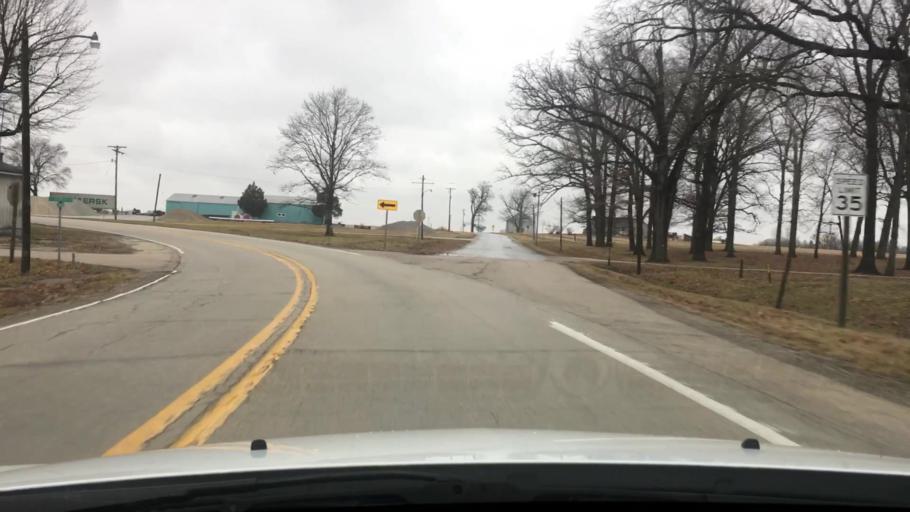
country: US
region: Illinois
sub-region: Iroquois County
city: Sheldon
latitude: 40.8281
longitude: -87.5817
